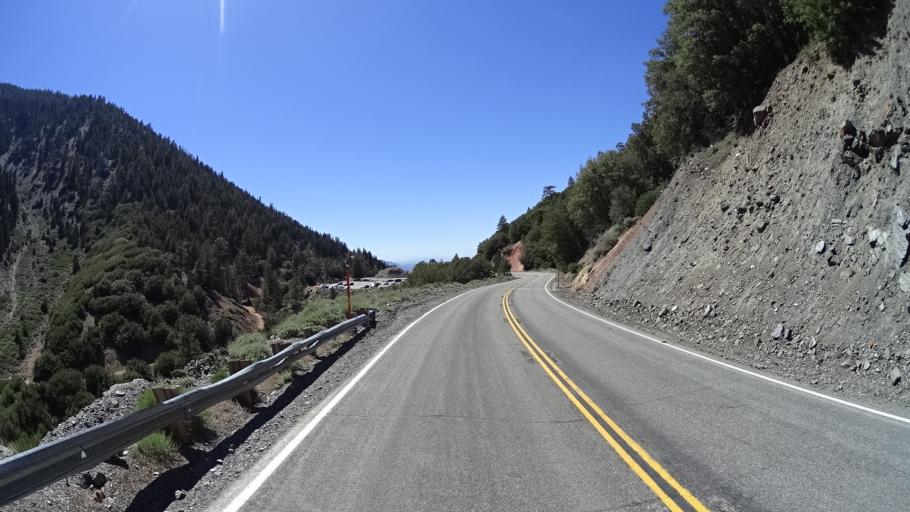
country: US
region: California
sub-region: San Bernardino County
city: Wrightwood
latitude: 34.3726
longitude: -117.7492
